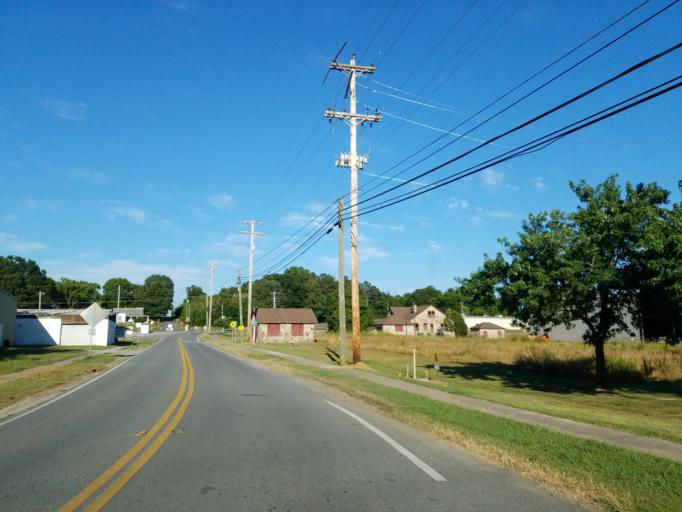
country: US
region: Georgia
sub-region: Gordon County
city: Calhoun
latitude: 34.5573
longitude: -85.0138
